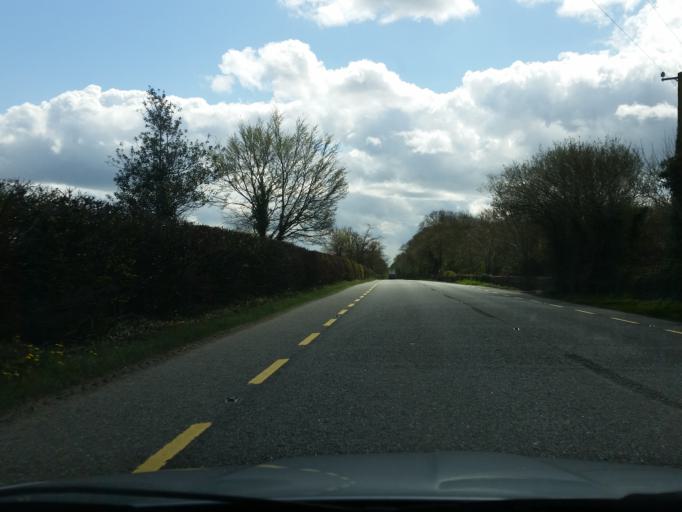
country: IE
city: Kentstown
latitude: 53.6355
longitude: -6.4949
